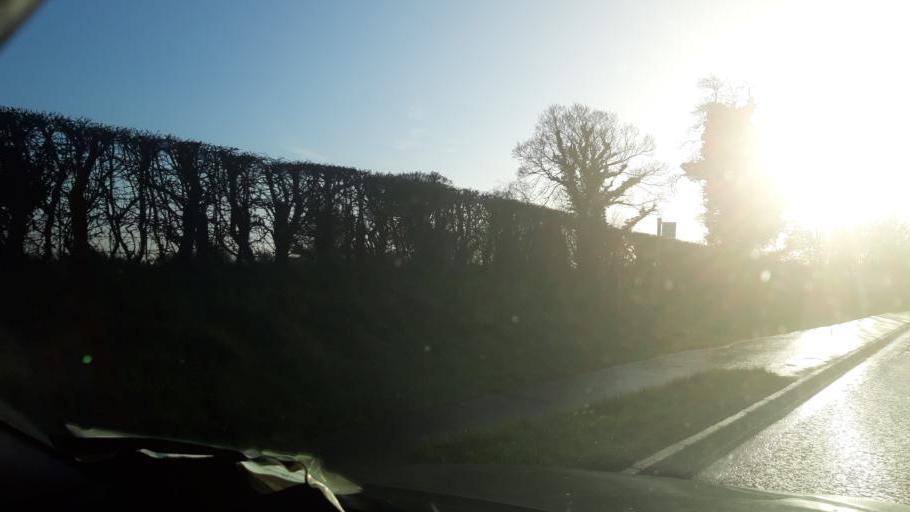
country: GB
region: Northern Ireland
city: Garvagh
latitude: 54.9915
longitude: -6.6834
